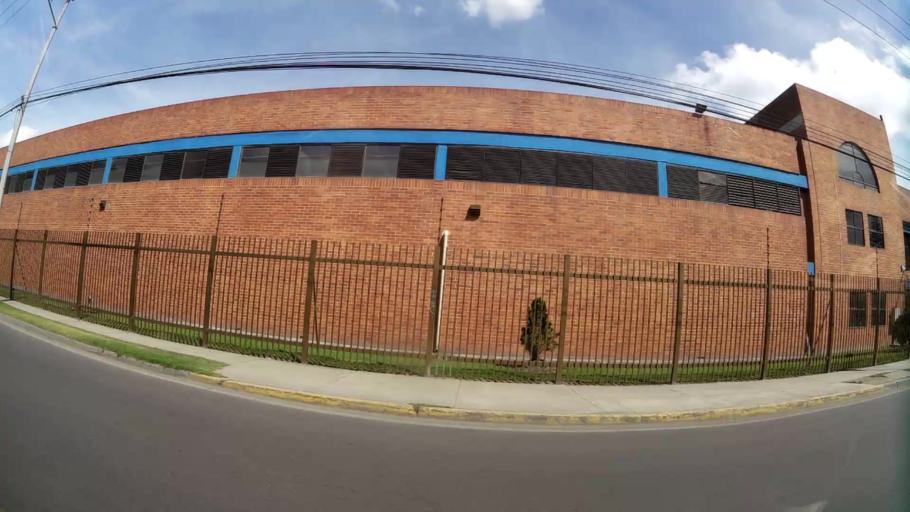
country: CO
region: Bogota D.C.
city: Bogota
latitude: 4.6487
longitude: -74.1366
